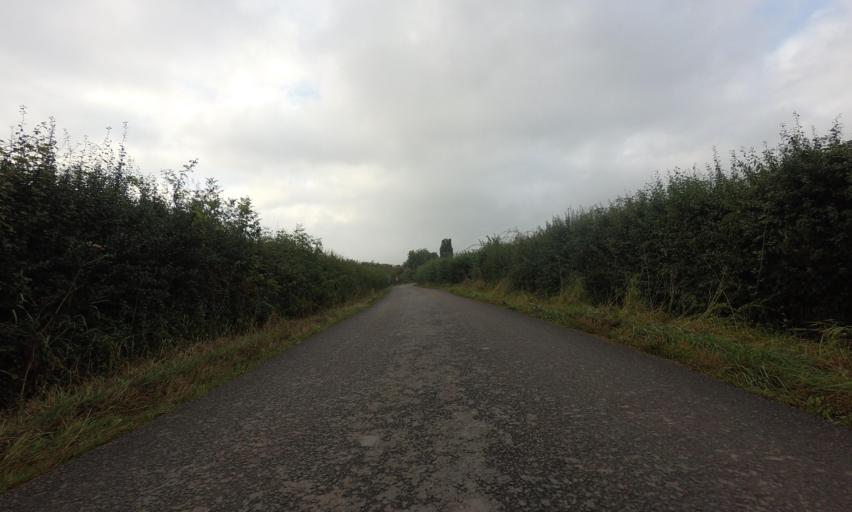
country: GB
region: England
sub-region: Gloucestershire
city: Gotherington
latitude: 51.9935
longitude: -2.0239
